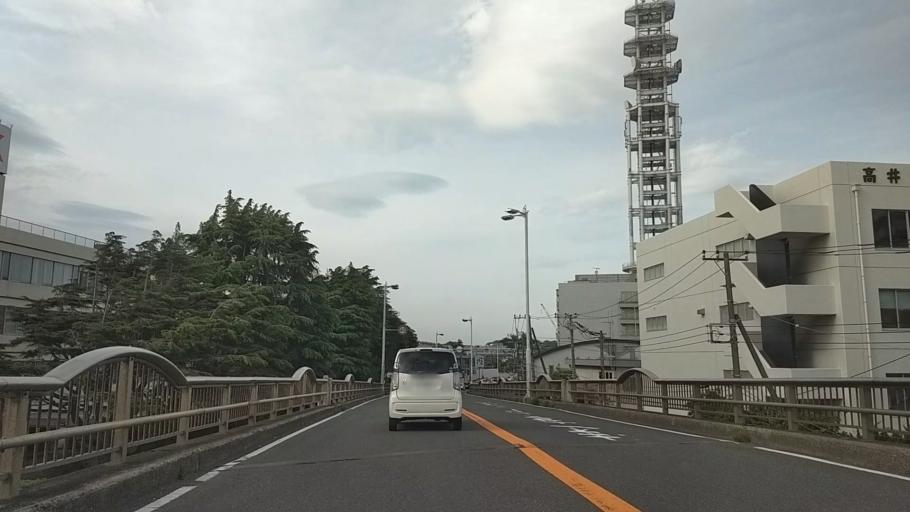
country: JP
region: Kanagawa
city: Fujisawa
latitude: 35.3385
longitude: 139.4767
